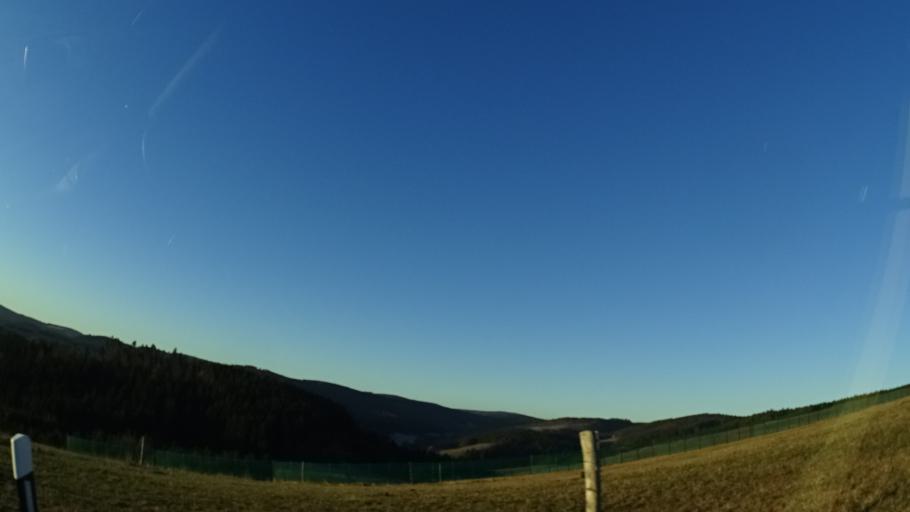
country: DE
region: Thuringia
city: Grafenthal
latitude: 50.5399
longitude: 11.2890
